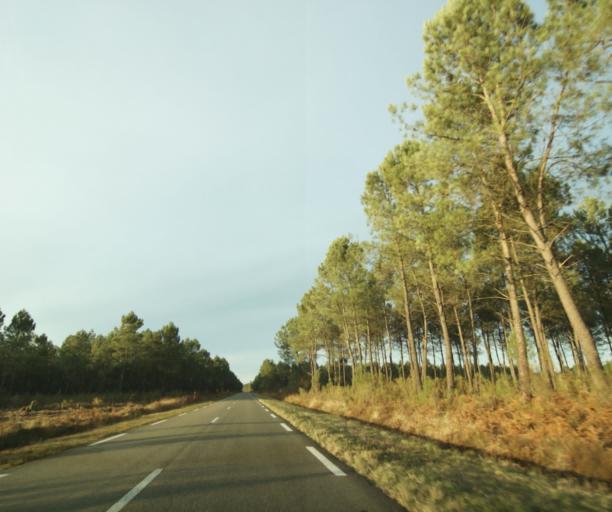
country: FR
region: Aquitaine
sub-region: Departement des Landes
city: Gabarret
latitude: 44.1612
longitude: -0.1341
